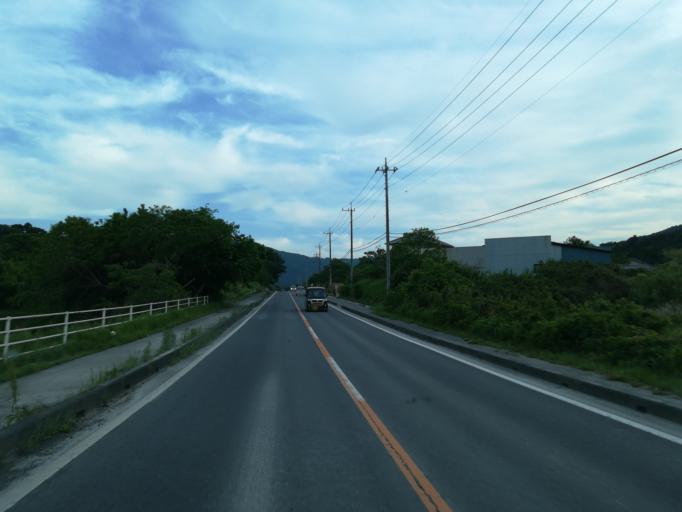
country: JP
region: Ibaraki
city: Tsukuba
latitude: 36.2045
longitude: 140.1792
